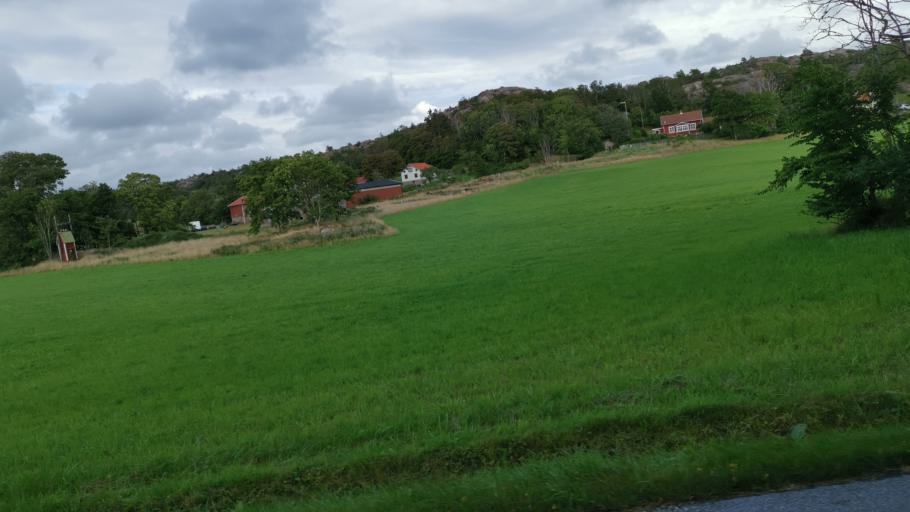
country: SE
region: Vaestra Goetaland
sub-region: Sotenas Kommun
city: Hunnebostrand
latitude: 58.5191
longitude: 11.3037
